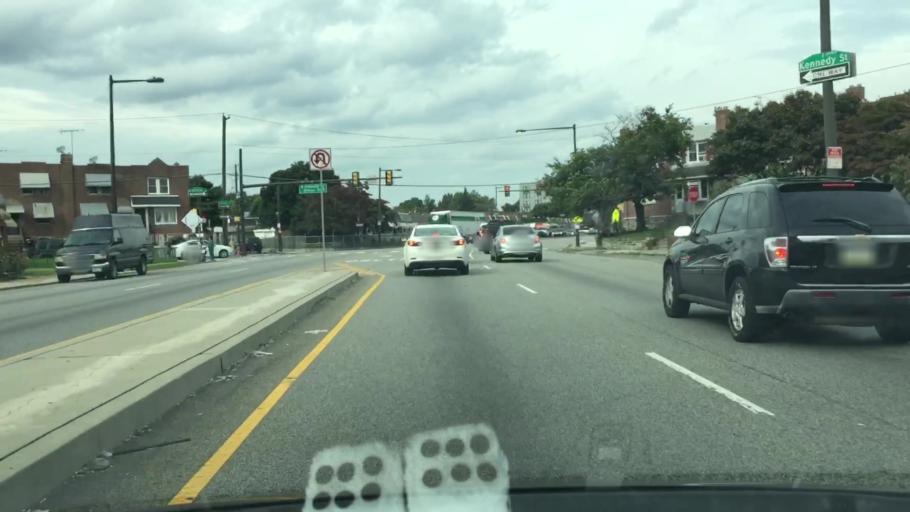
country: US
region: New Jersey
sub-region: Burlington County
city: Palmyra
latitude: 40.0142
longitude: -75.0684
